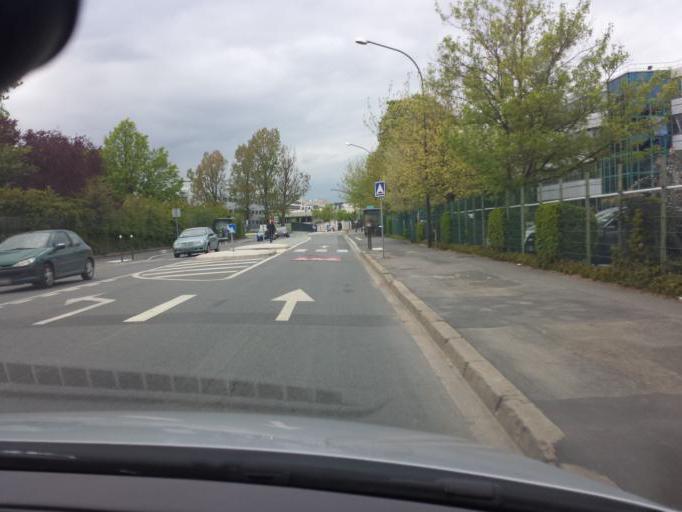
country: FR
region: Ile-de-France
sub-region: Departement de l'Essonne
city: Massy
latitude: 48.7239
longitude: 2.2696
